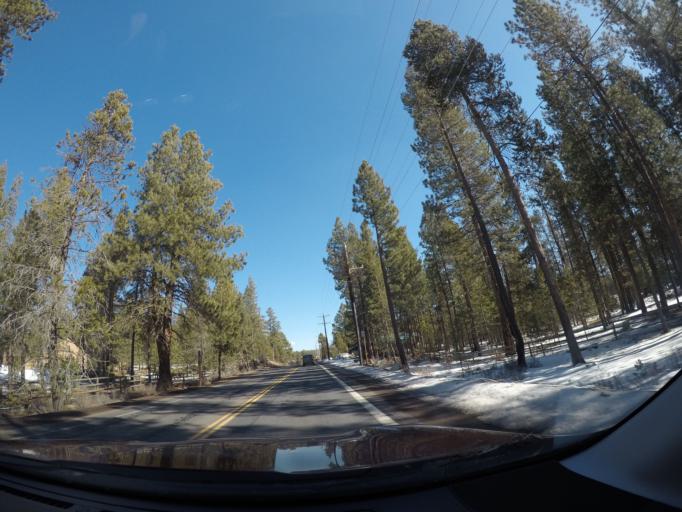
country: US
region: Oregon
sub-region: Deschutes County
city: Sunriver
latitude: 43.8633
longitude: -121.4430
